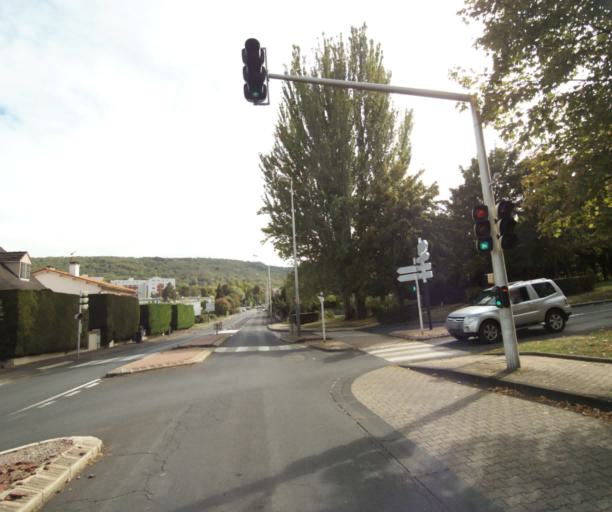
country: FR
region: Auvergne
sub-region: Departement du Puy-de-Dome
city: Romagnat
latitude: 45.7334
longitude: 3.0984
